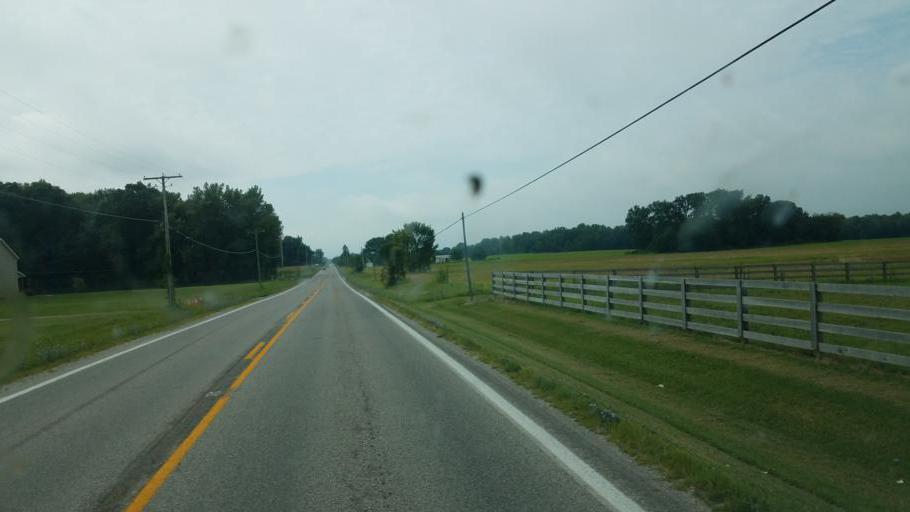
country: US
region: Ohio
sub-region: Morrow County
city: Cardington
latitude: 40.4136
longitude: -82.8259
